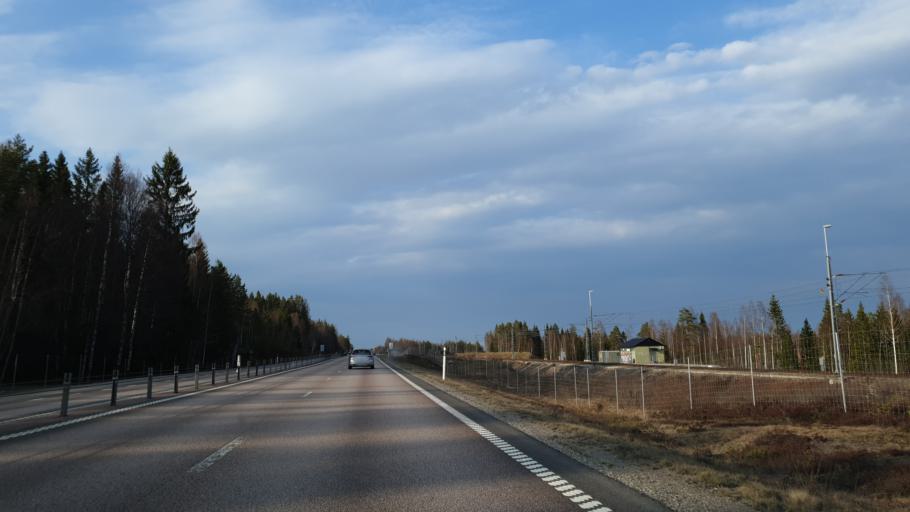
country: SE
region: Gaevleborg
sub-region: Hudiksvalls Kommun
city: Hudiksvall
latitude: 61.8426
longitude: 17.1976
